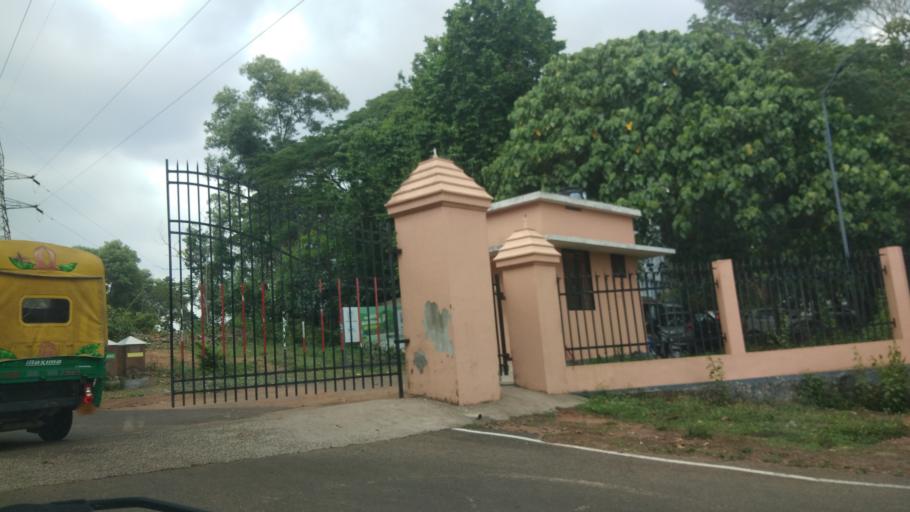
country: IN
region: Kerala
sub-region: Ernakulam
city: Elur
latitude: 10.0439
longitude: 76.3260
